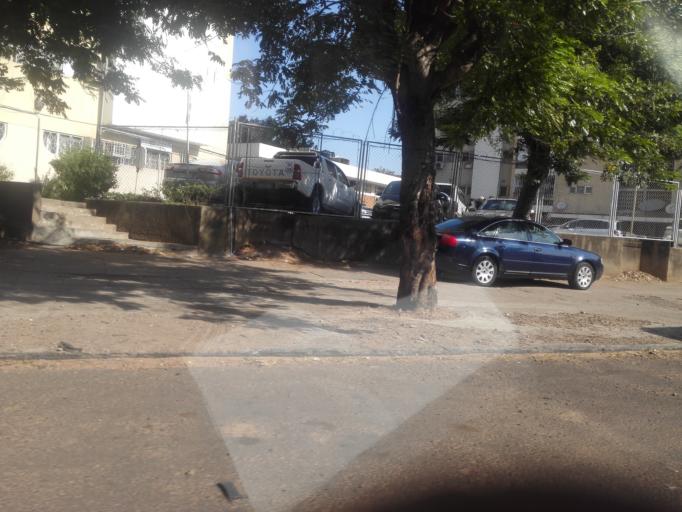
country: MZ
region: Maputo City
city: Maputo
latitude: -25.9550
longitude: 32.5872
